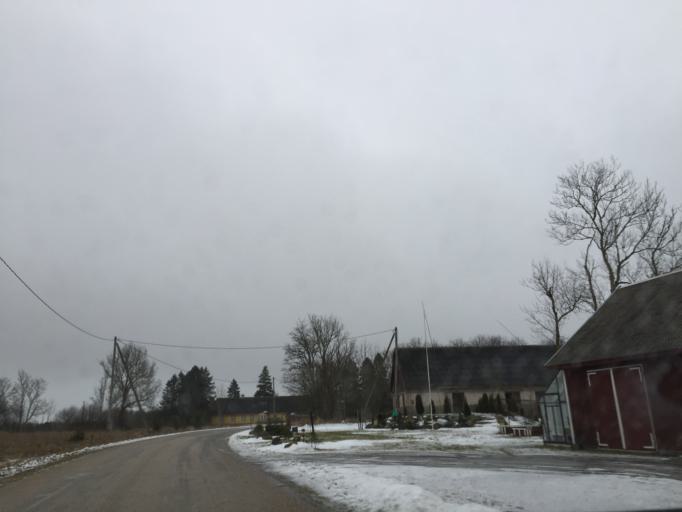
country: EE
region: Laeaene
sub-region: Lihula vald
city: Lihula
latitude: 58.5801
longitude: 23.5401
